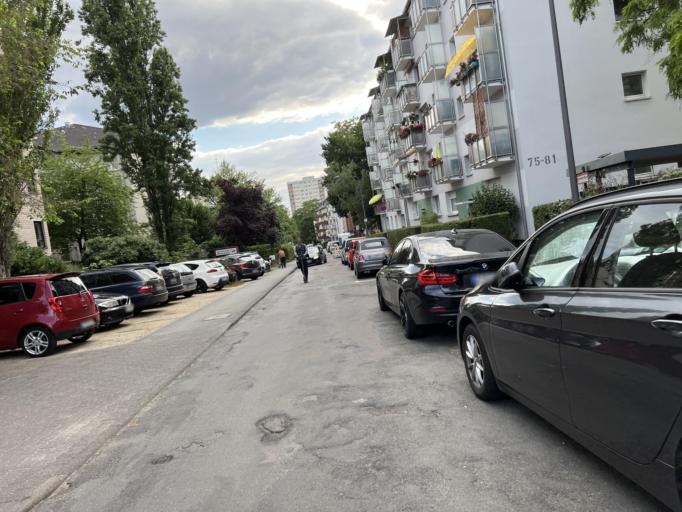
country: DE
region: Hesse
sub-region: Regierungsbezirk Darmstadt
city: Frankfurt am Main
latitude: 50.1153
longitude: 8.7076
